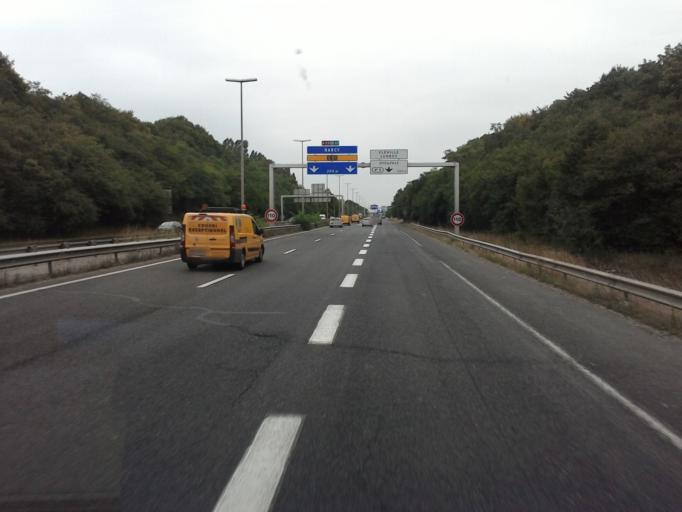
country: FR
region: Lorraine
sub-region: Departement de Meurthe-et-Moselle
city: Richardmenil
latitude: 48.6123
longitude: 6.1774
